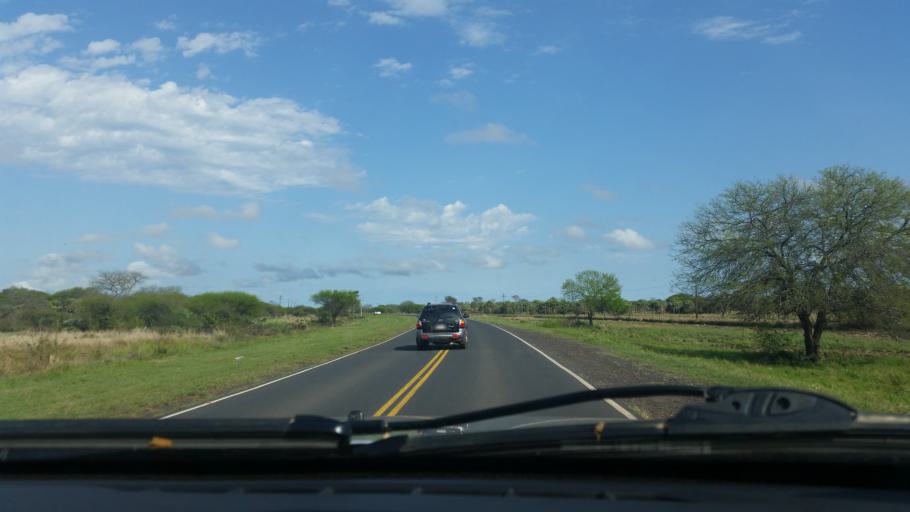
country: PY
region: Presidente Hayes
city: Benjamin Aceval
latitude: -24.9225
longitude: -57.5750
